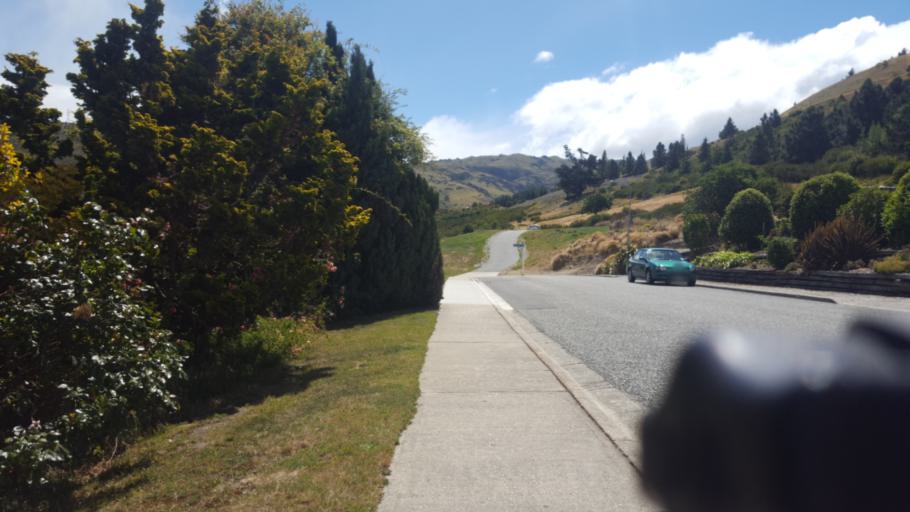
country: NZ
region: Otago
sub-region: Queenstown-Lakes District
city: Wanaka
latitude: -45.1865
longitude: 169.3234
